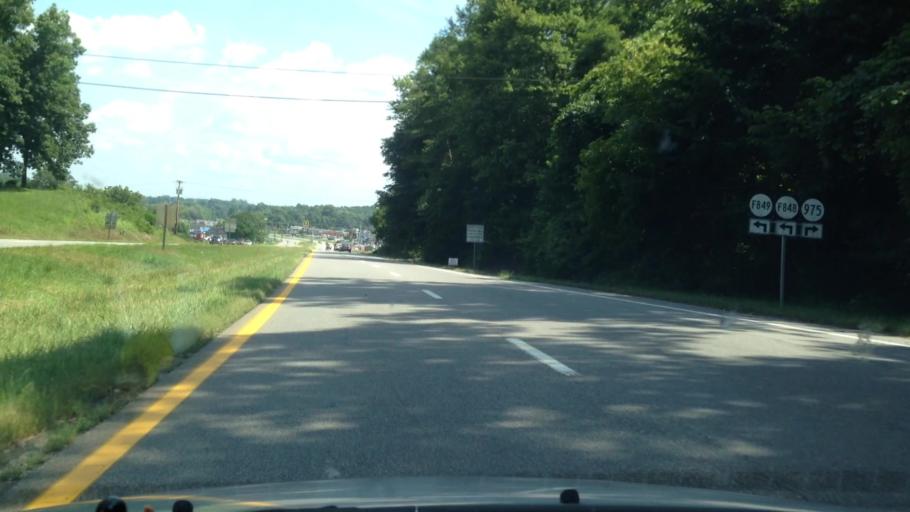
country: US
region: Virginia
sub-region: City of Martinsville
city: Martinsville
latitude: 36.6594
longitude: -79.8811
